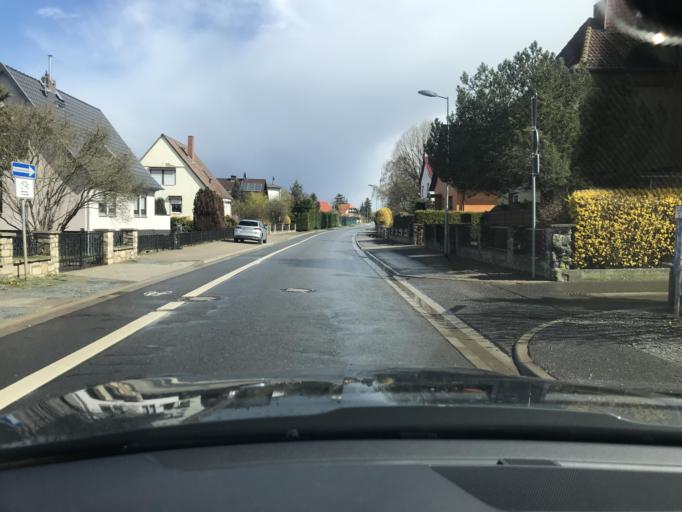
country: DE
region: Saxony-Anhalt
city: Hoym
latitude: 51.7296
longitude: 11.3480
